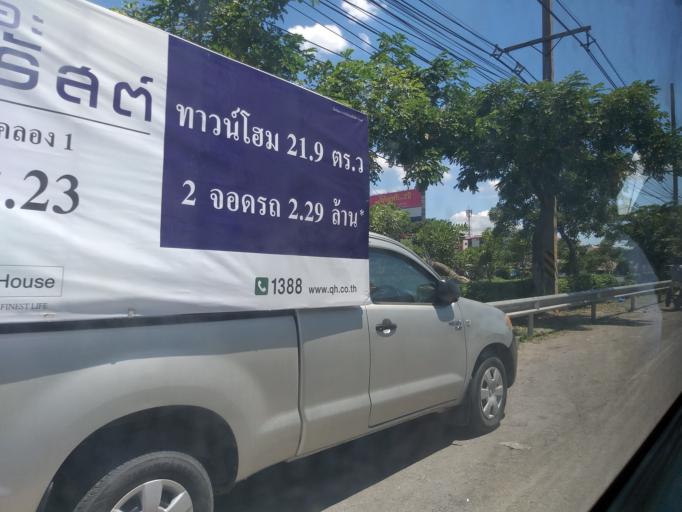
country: TH
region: Bangkok
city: Sai Mai
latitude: 13.9877
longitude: 100.6328
